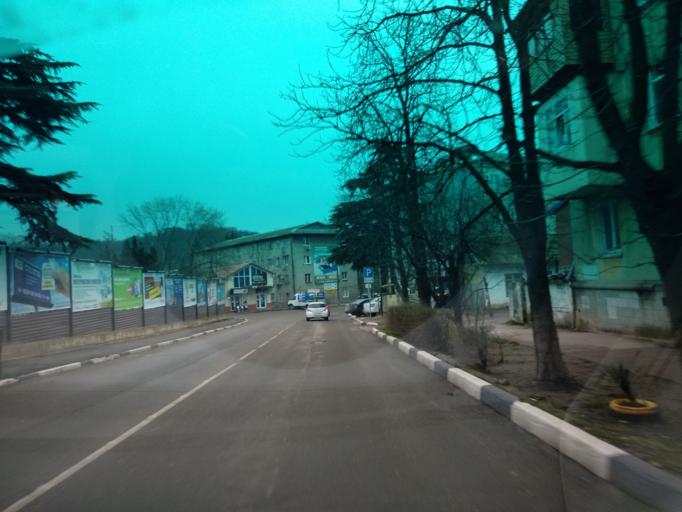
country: RU
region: Krasnodarskiy
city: Tuapse
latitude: 44.1004
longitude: 39.0834
